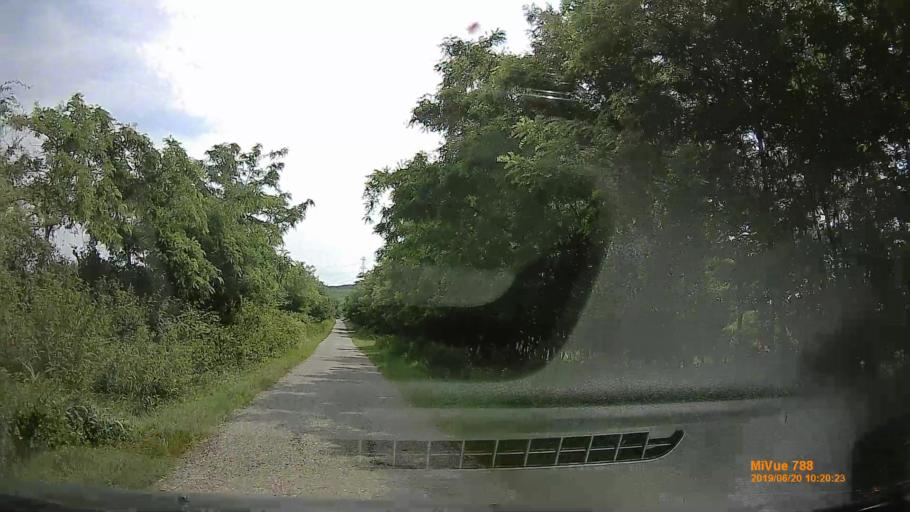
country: HU
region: Baranya
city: Mecseknadasd
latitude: 46.2102
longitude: 18.4678
